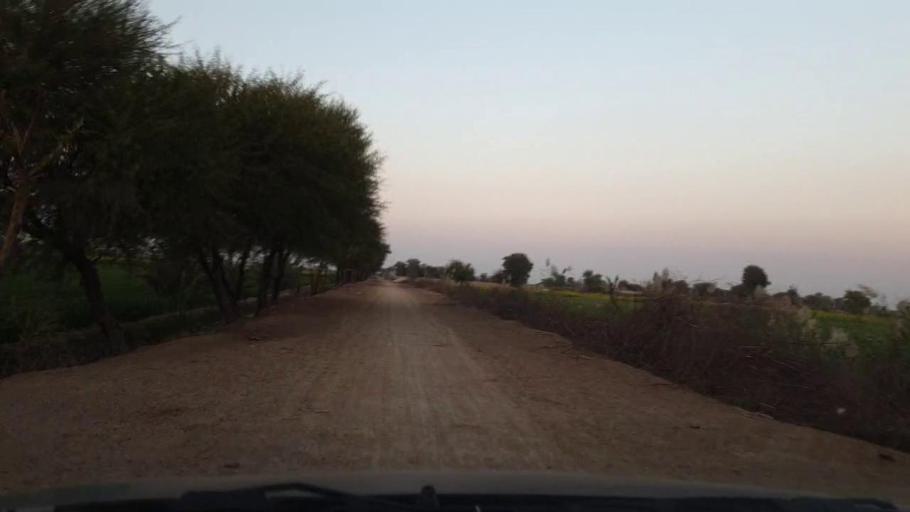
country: PK
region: Sindh
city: Jhol
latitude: 25.9378
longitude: 68.9685
